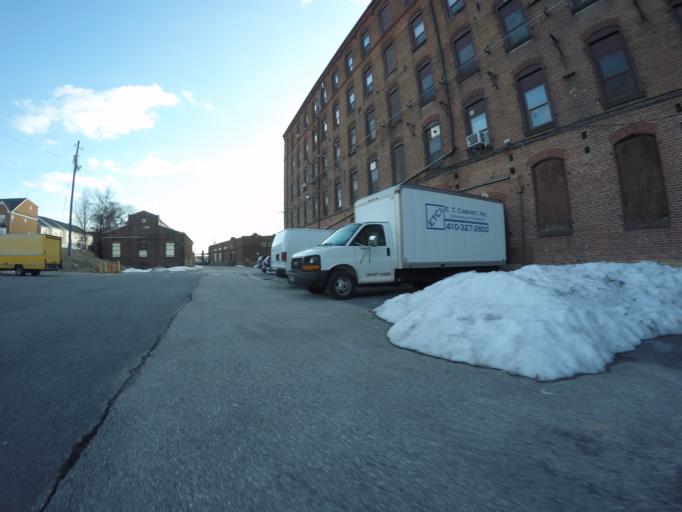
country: US
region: Maryland
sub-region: Baltimore County
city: Dundalk
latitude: 39.2856
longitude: -76.5584
